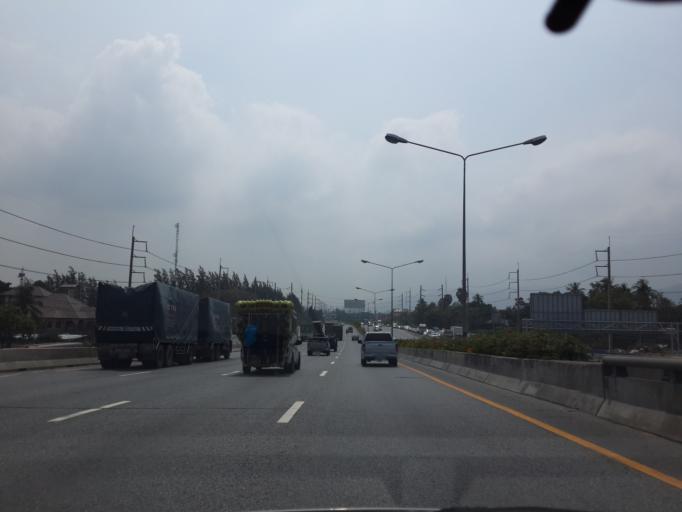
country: TH
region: Chon Buri
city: Chon Buri
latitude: 13.3863
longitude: 101.0159
